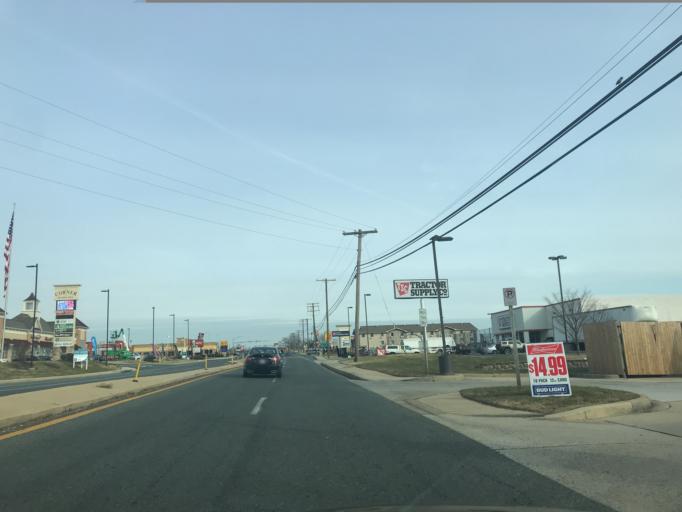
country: US
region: Maryland
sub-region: Harford County
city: Aberdeen
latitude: 39.5197
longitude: -76.1856
